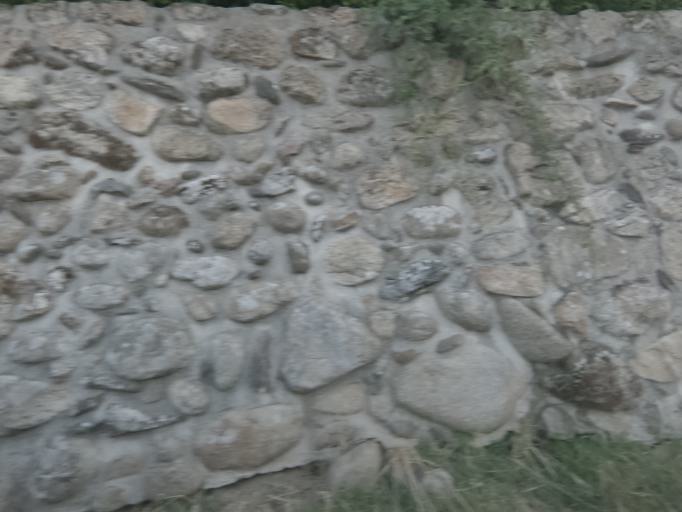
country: PT
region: Vila Real
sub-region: Vila Real
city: Vila Real
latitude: 41.3154
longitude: -7.7615
